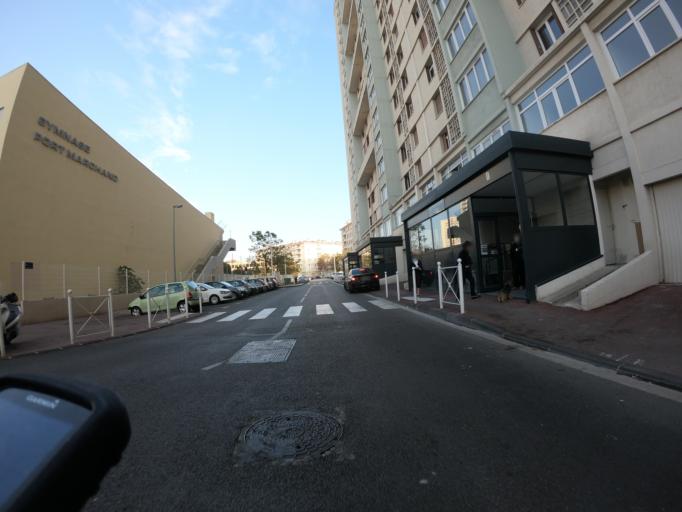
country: FR
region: Provence-Alpes-Cote d'Azur
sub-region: Departement du Var
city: Toulon
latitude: 43.1130
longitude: 5.9358
